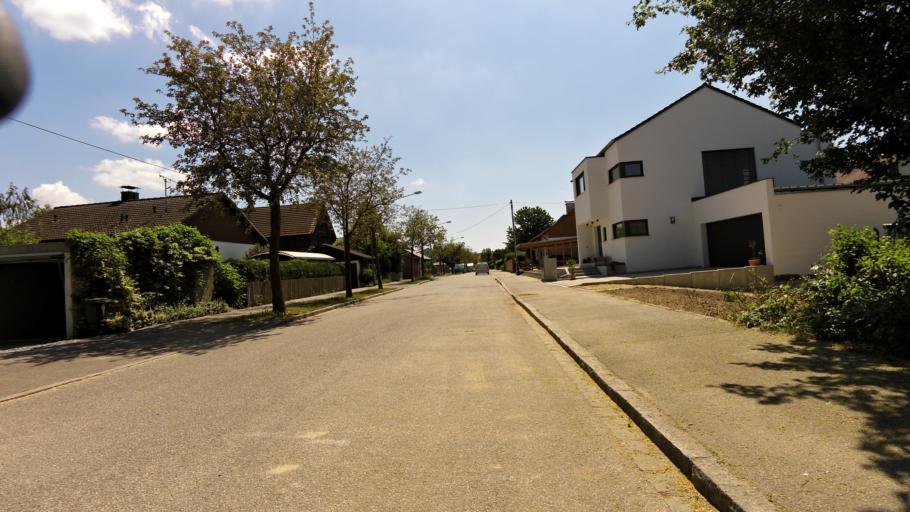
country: DE
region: Bavaria
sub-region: Lower Bavaria
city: Tiefenbach
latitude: 48.5360
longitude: 12.0911
